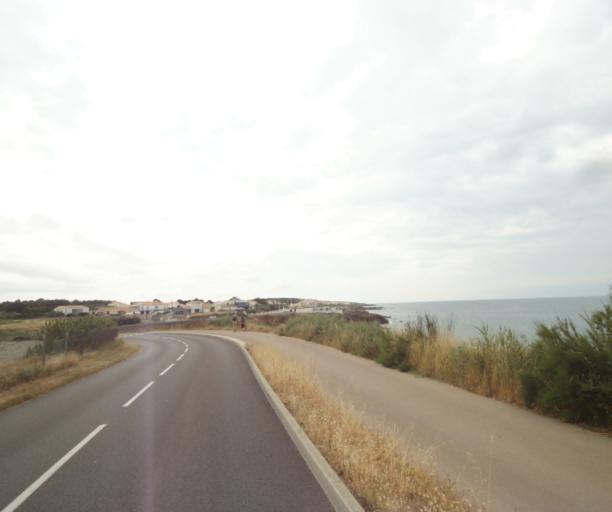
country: FR
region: Pays de la Loire
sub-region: Departement de la Vendee
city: Chateau-d'Olonne
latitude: 46.4684
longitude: -1.7393
